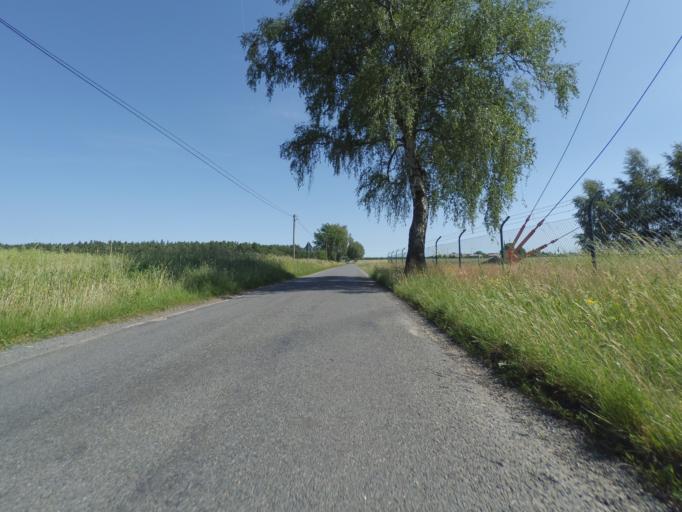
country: DE
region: Brandenburg
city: Pritzwalk
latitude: 53.1058
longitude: 12.1794
